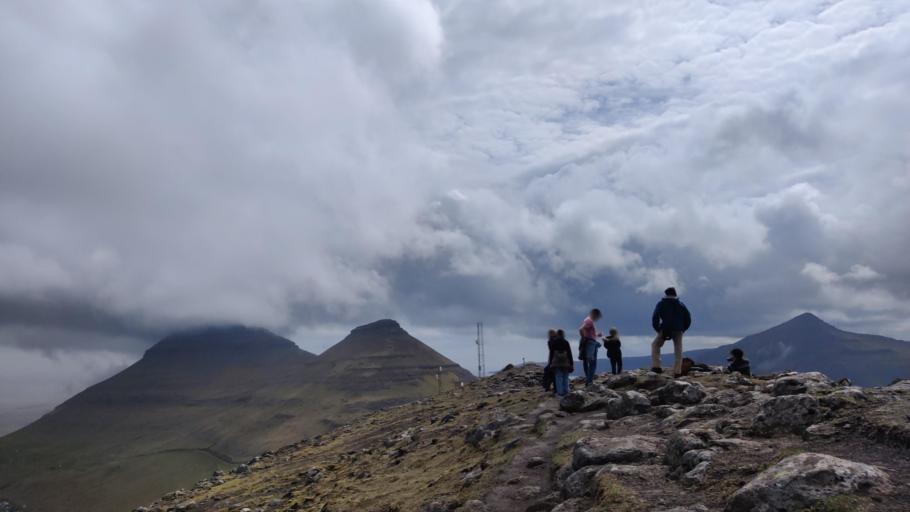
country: FO
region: Nordoyar
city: Klaksvik
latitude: 62.2363
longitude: -6.6168
